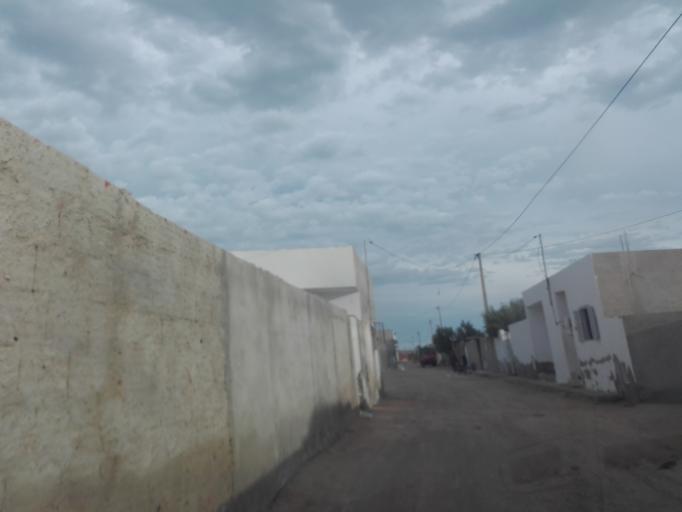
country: TN
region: Safaqis
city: Al Qarmadah
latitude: 34.8076
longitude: 10.8603
